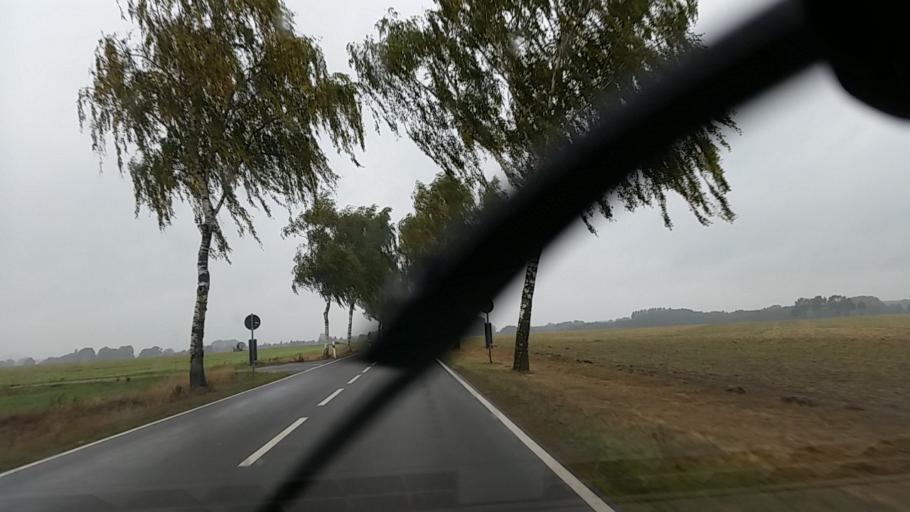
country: DE
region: Lower Saxony
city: Wittingen
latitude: 52.7529
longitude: 10.7210
